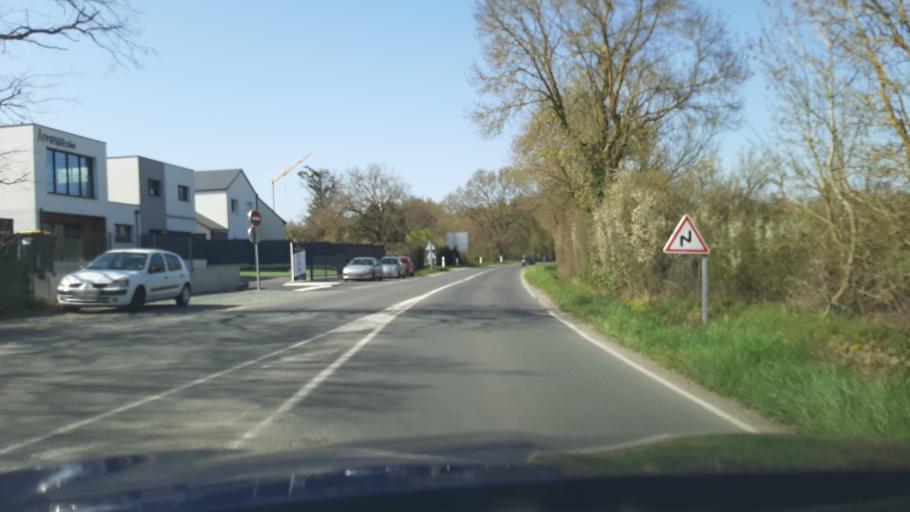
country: FR
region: Pays de la Loire
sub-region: Departement de Maine-et-Loire
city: Les Ponts-de-Ce
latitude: 47.4009
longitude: -0.5157
